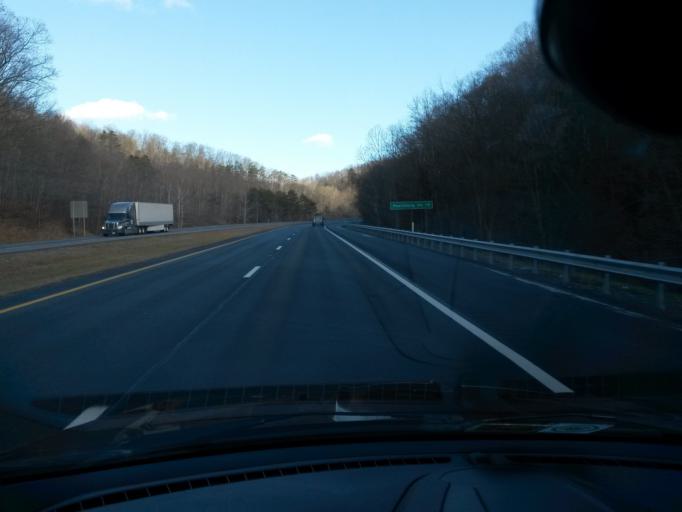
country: US
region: West Virginia
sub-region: Mercer County
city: Athens
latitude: 37.3460
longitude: -80.9460
